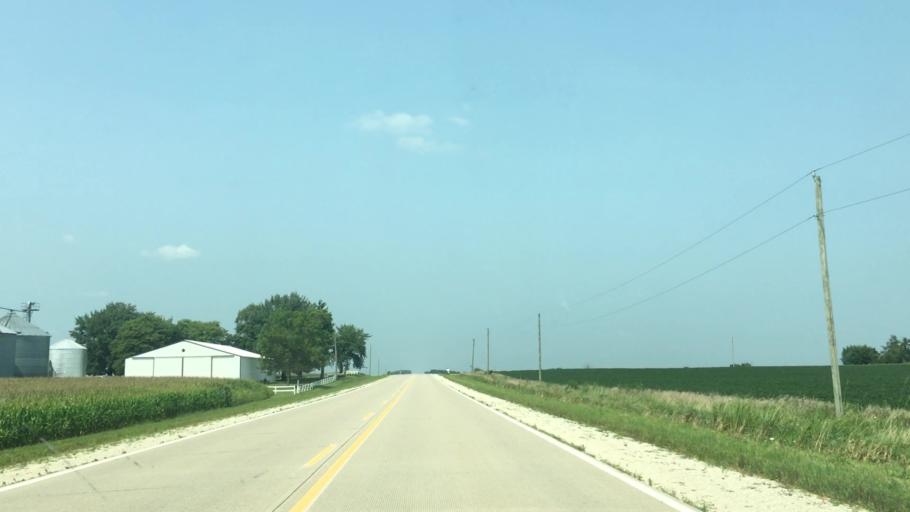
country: US
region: Iowa
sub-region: Fayette County
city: Fayette
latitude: 42.7429
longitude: -91.8041
